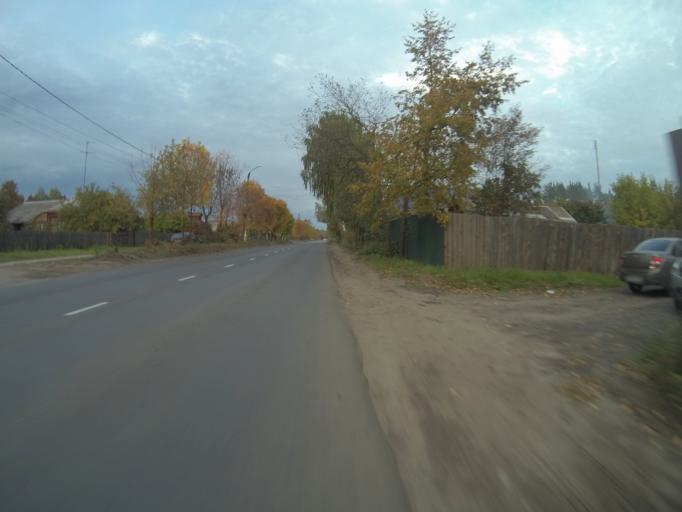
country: RU
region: Vladimir
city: Sobinka
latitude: 55.9982
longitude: 40.0397
